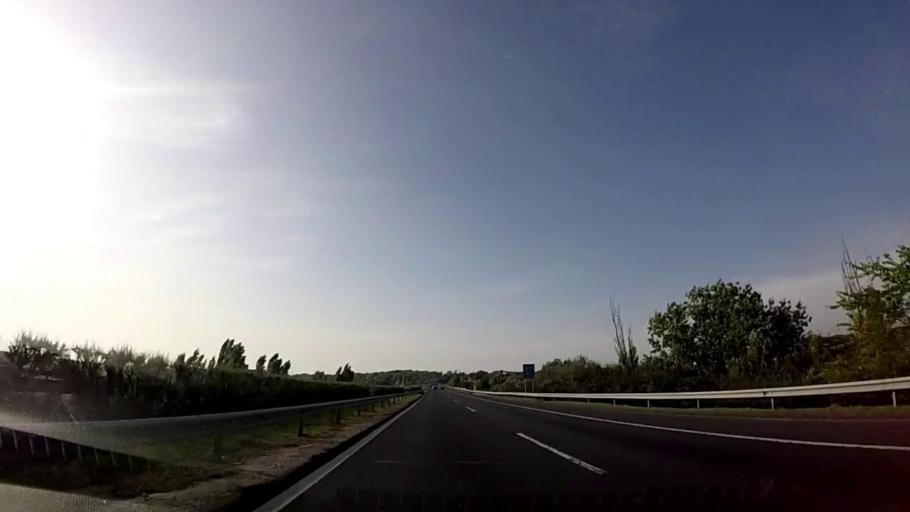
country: HU
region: Fejer
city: Baracska
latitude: 47.3030
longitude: 18.7422
